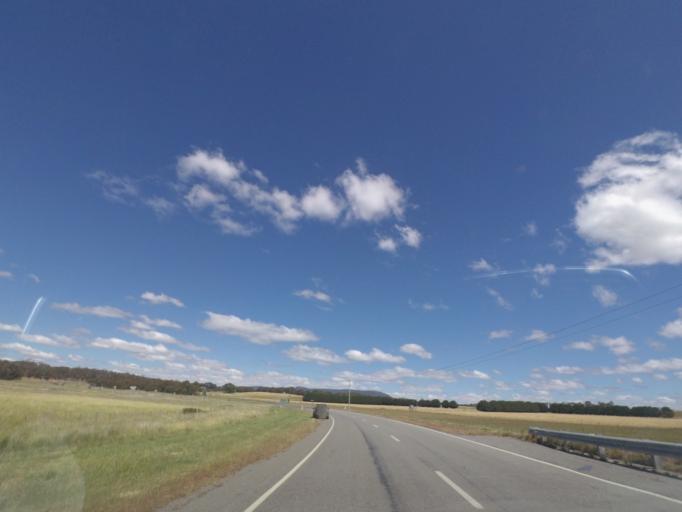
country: AU
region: Victoria
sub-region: Hume
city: Sunbury
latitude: -37.2954
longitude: 144.4989
